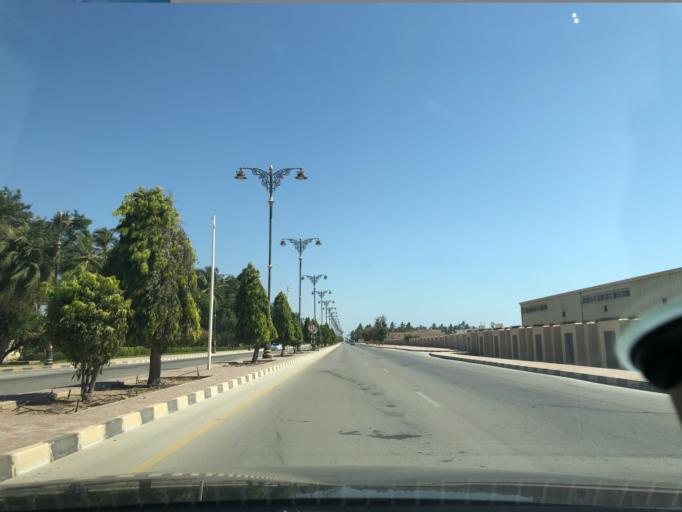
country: OM
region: Zufar
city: Salalah
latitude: 17.0261
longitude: 54.1479
